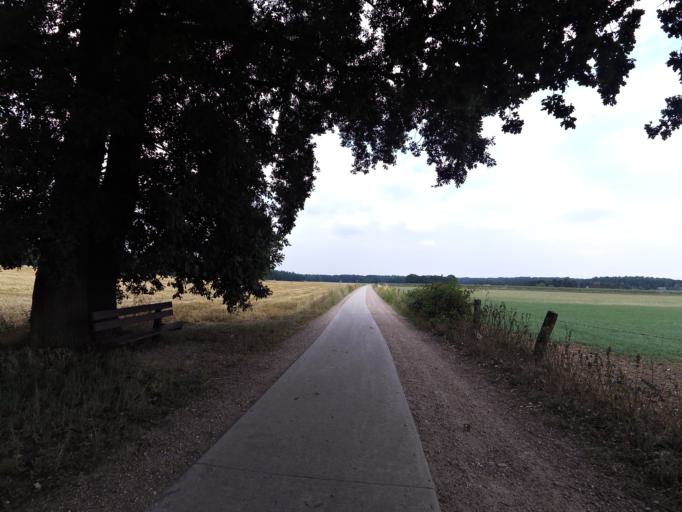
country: NL
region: Gelderland
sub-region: Gemeente Montferland
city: s-Heerenberg
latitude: 51.8843
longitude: 6.2142
